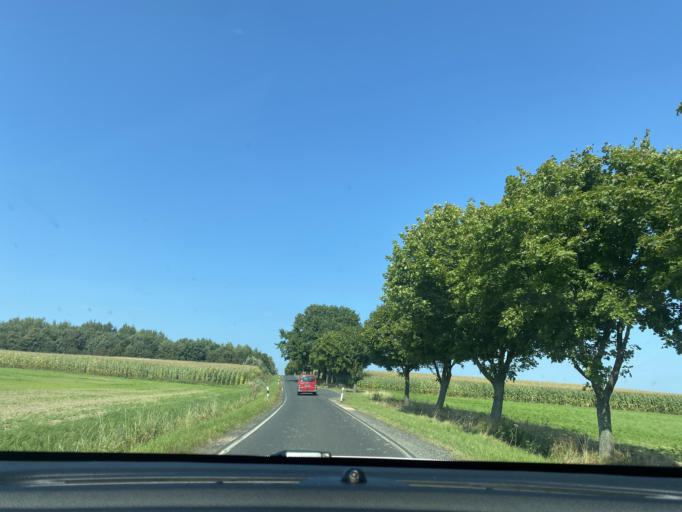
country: DE
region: Saxony
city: Quitzdorf
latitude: 51.2266
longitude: 14.7745
